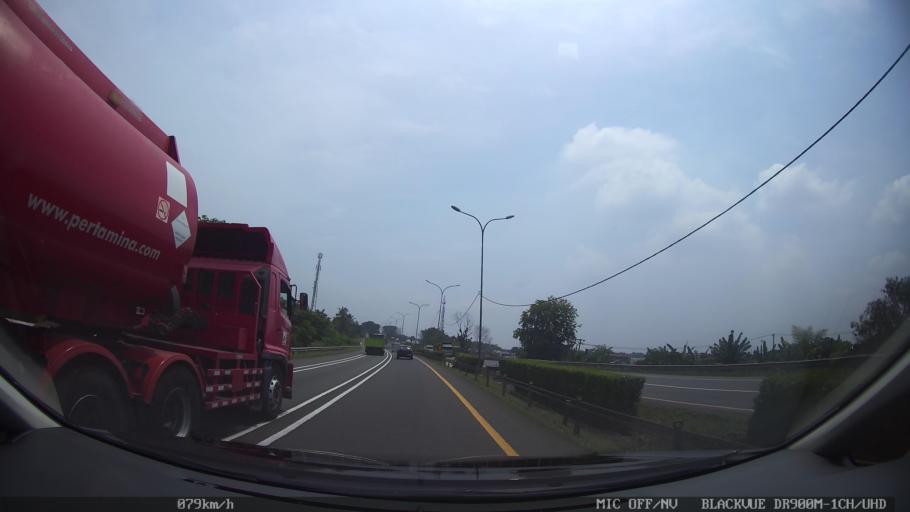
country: ID
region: West Java
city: Kresek
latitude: -6.1525
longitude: 106.3178
